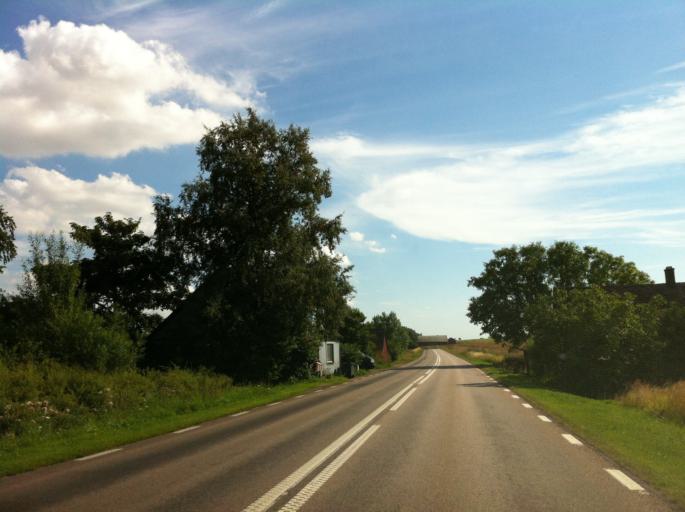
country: SE
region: Skane
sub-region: Landskrona
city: Asmundtorp
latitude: 55.9756
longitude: 12.9369
